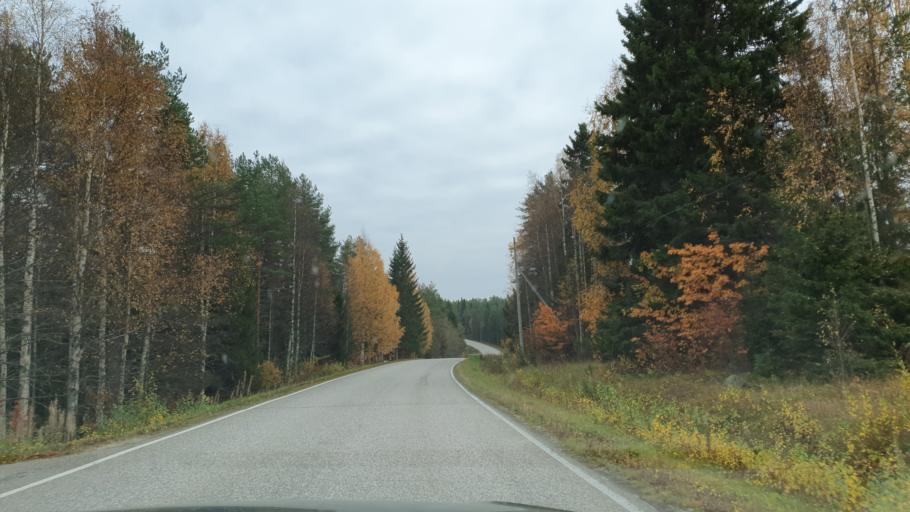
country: FI
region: Kainuu
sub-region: Kajaani
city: Ristijaervi
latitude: 64.4536
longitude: 28.3494
